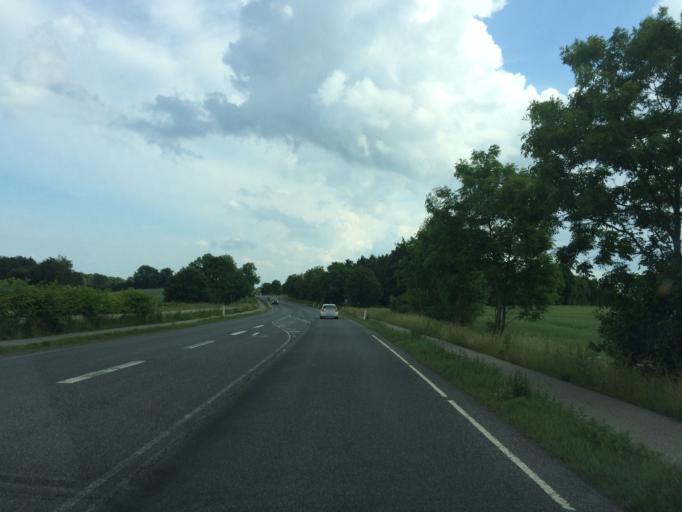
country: DK
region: South Denmark
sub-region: Vejle Kommune
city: Borkop
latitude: 55.5969
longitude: 9.6338
